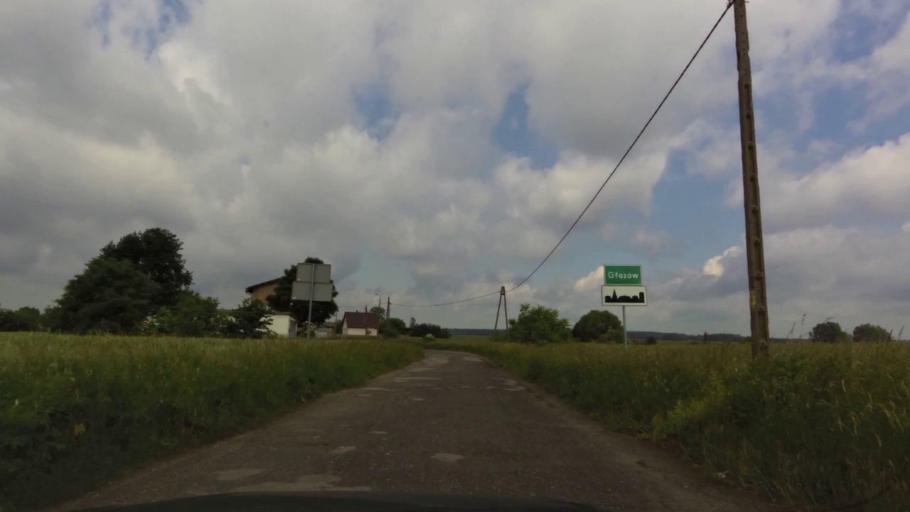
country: PL
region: West Pomeranian Voivodeship
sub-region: Powiat pyrzycki
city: Lipiany
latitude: 52.9633
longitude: 14.9619
